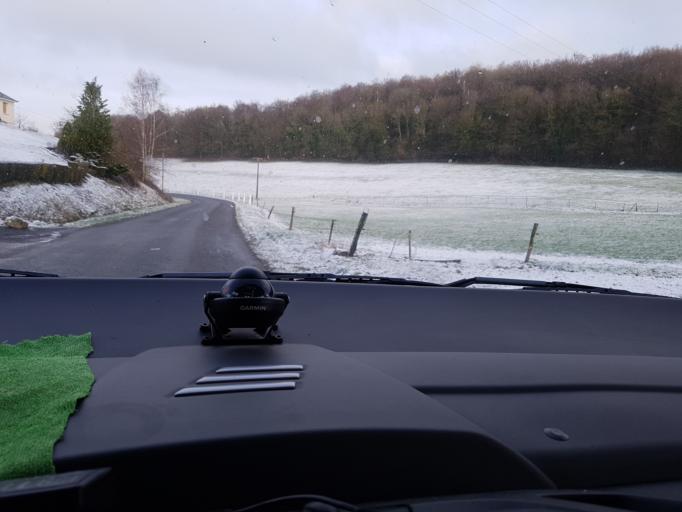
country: FR
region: Champagne-Ardenne
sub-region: Departement des Ardennes
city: Tournes
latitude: 49.7271
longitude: 4.5650
